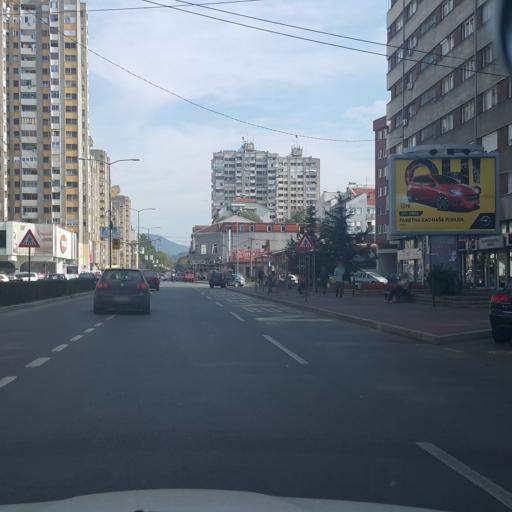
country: RS
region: Central Serbia
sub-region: Nisavski Okrug
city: Nis
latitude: 43.3194
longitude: 21.9075
